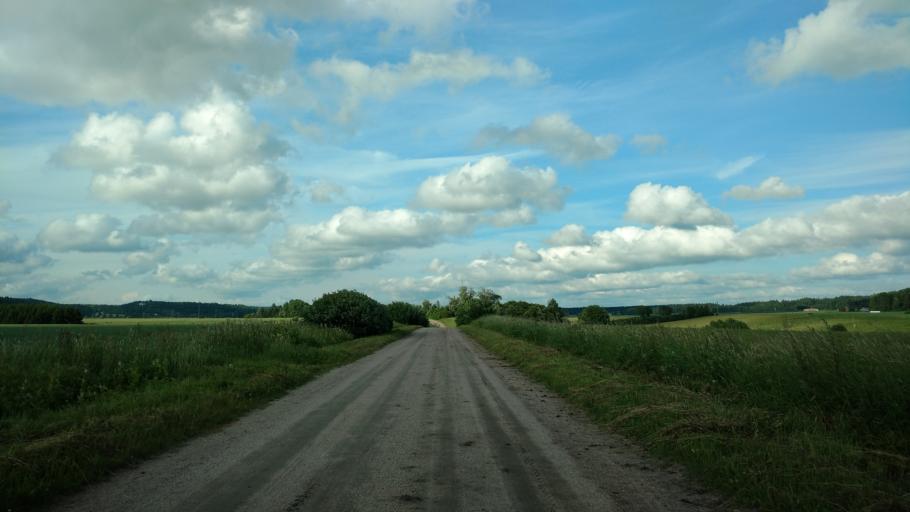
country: FI
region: Varsinais-Suomi
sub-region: Salo
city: Salo
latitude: 60.4055
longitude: 23.1608
